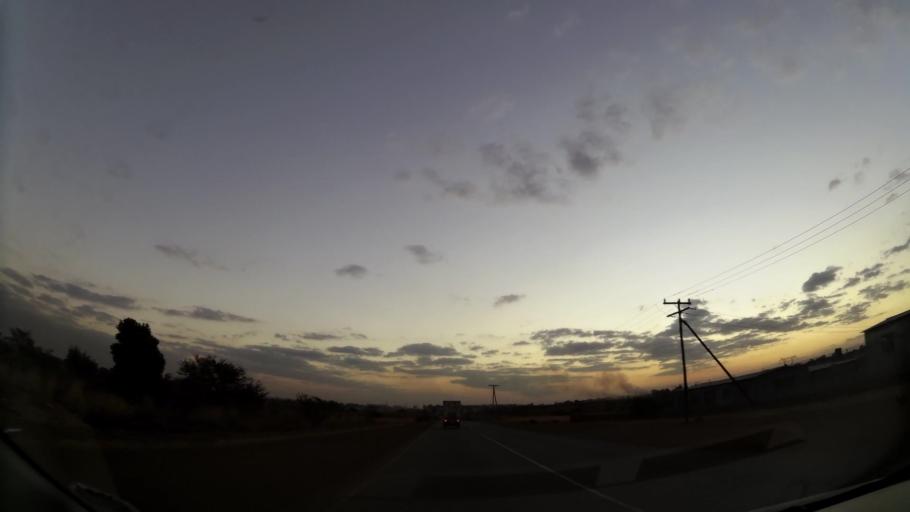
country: ZA
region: Gauteng
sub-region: West Rand District Municipality
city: Krugersdorp
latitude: -26.0718
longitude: 27.6643
